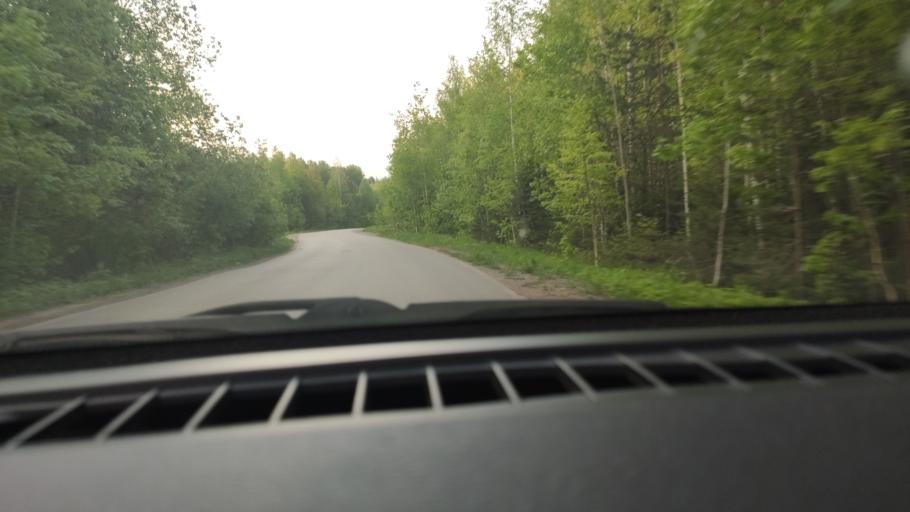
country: RU
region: Perm
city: Kondratovo
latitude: 58.0659
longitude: 56.0021
